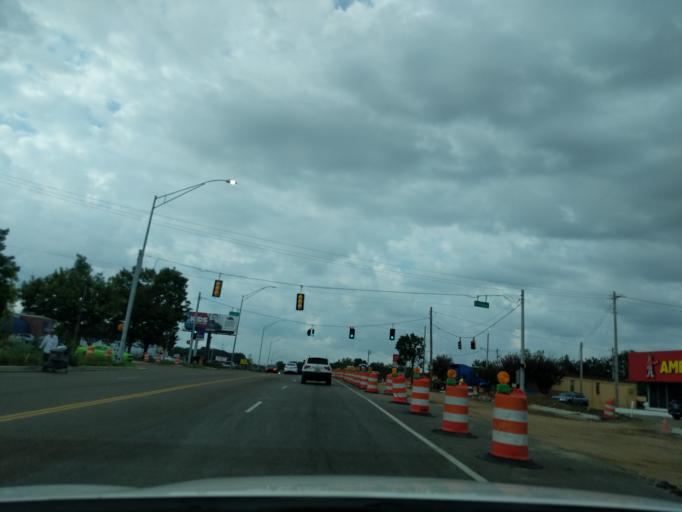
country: US
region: Tennessee
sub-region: Shelby County
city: New South Memphis
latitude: 35.0587
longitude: -90.0242
